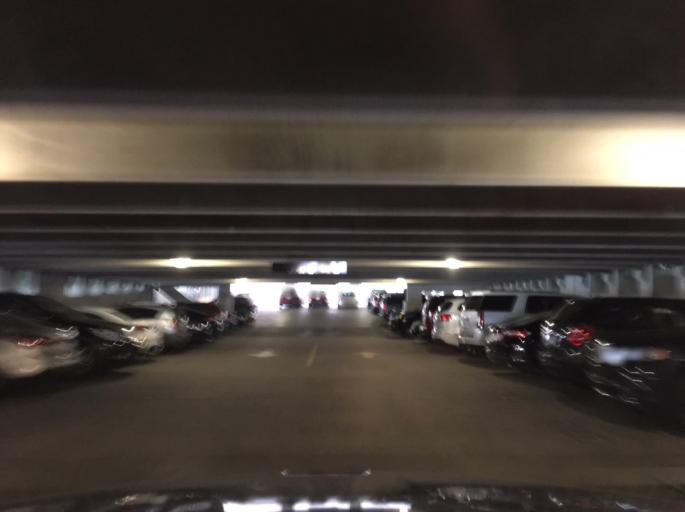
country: US
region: Michigan
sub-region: Wayne County
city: Detroit
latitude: 42.3307
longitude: -83.0374
